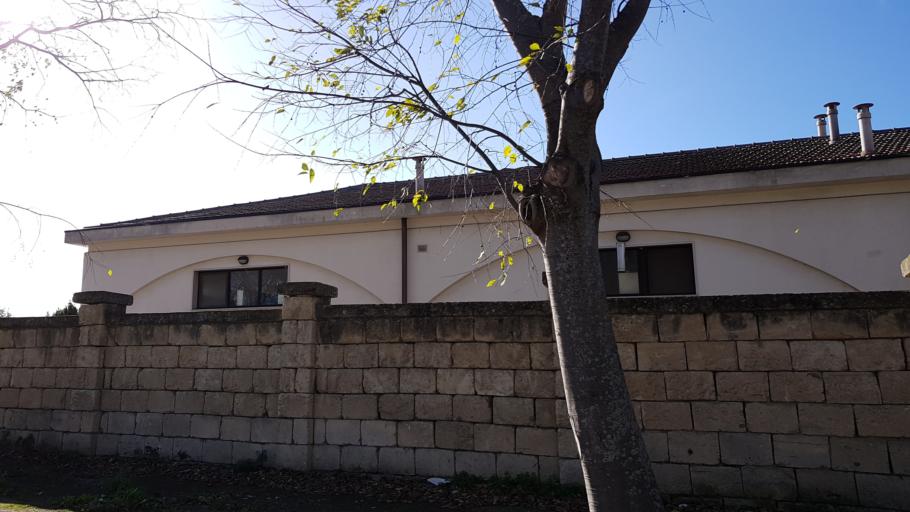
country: IT
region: Apulia
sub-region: Provincia di Foggia
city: Carapelle
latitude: 41.3821
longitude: 15.6426
